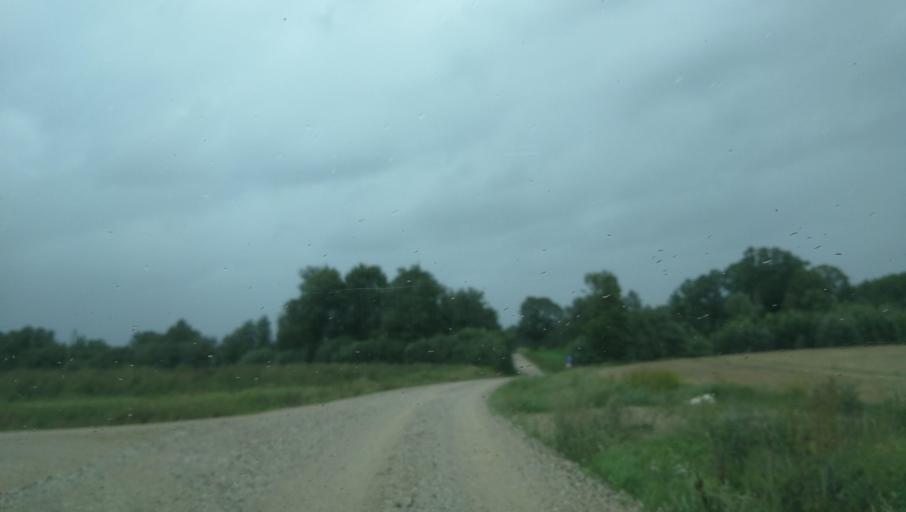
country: LV
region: Beverina
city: Murmuiza
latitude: 57.4084
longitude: 25.4602
